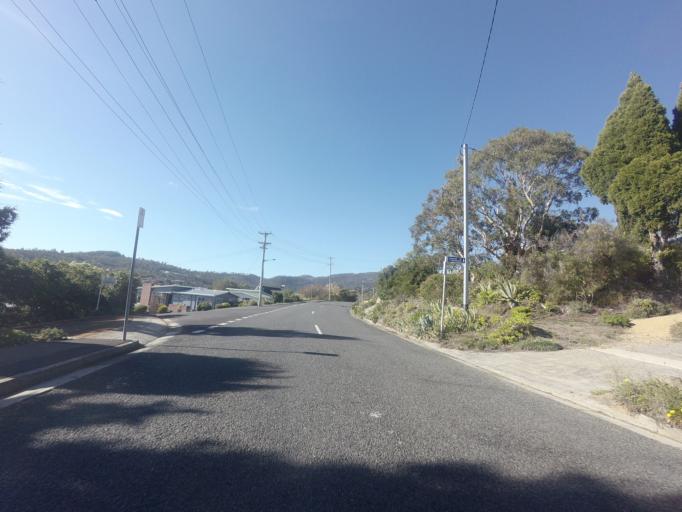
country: AU
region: Tasmania
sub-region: Clarence
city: Lindisfarne
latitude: -42.8403
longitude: 147.3482
